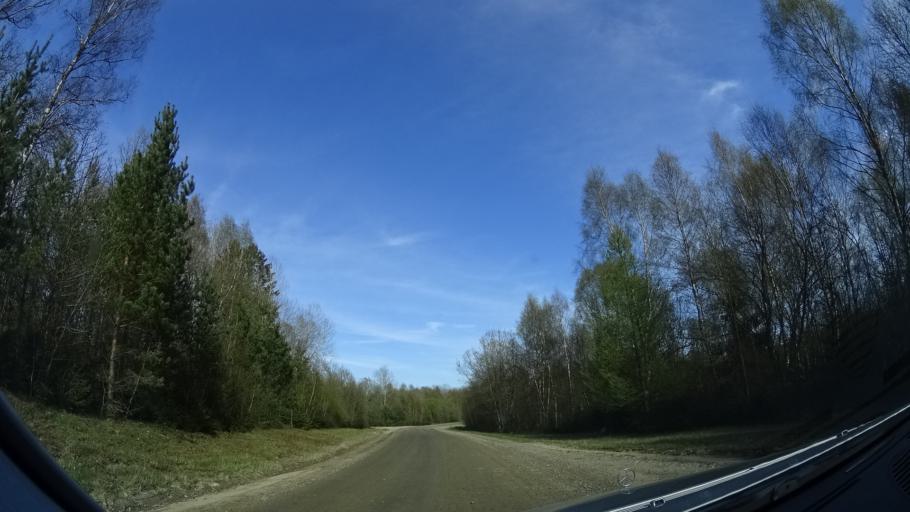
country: SE
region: Skane
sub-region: Hassleholms Kommun
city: Sosdala
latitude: 56.0873
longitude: 13.6726
